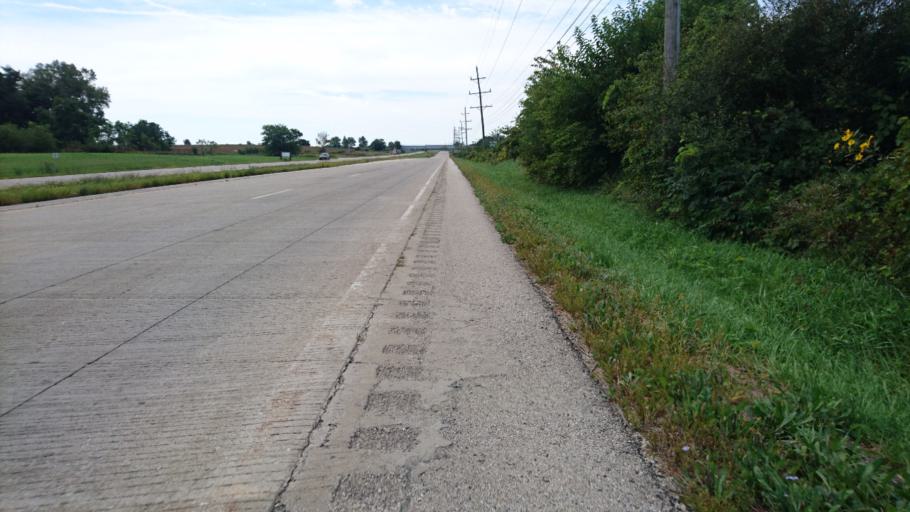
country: US
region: Illinois
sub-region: Will County
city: Elwood
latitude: 41.3802
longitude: -88.1264
